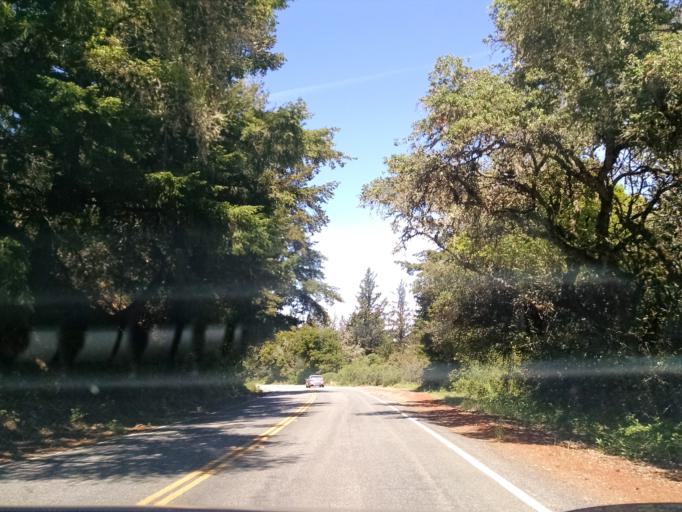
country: US
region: California
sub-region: San Mateo County
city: Portola Valley
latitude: 37.3472
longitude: -122.2300
